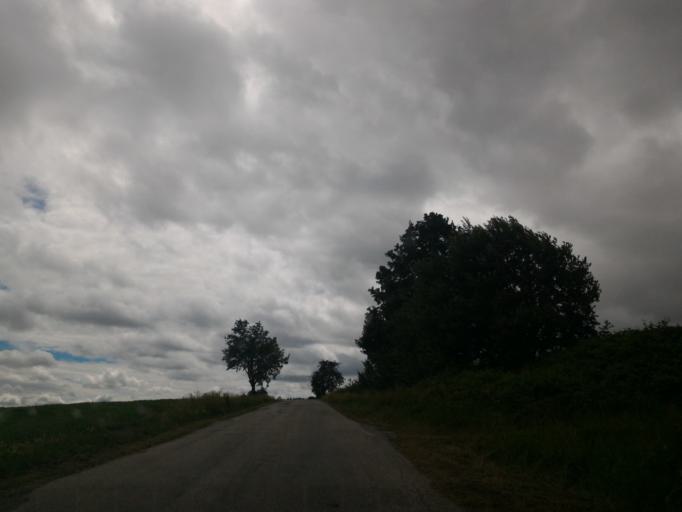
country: CZ
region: Vysocina
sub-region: Okres Jihlava
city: Telc
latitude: 49.2302
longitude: 15.4264
